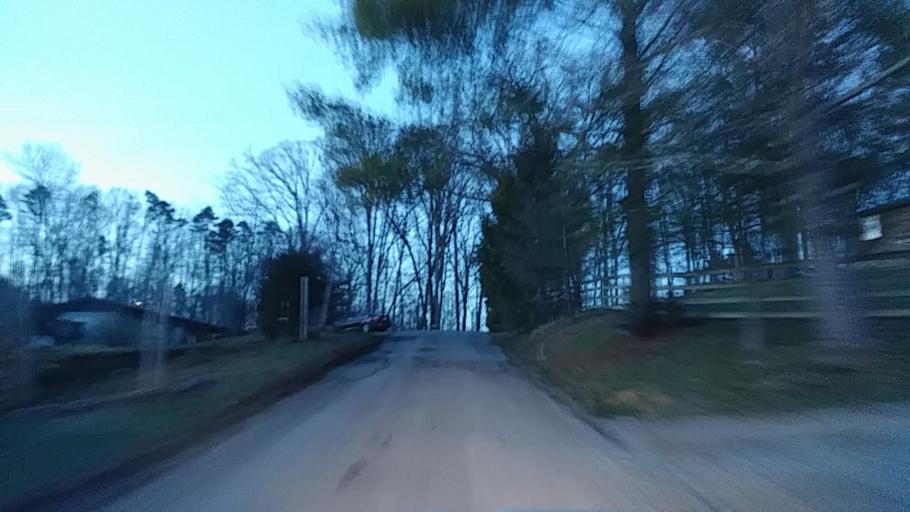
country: US
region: Tennessee
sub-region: Greene County
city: Mosheim
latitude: 36.0739
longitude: -82.9898
